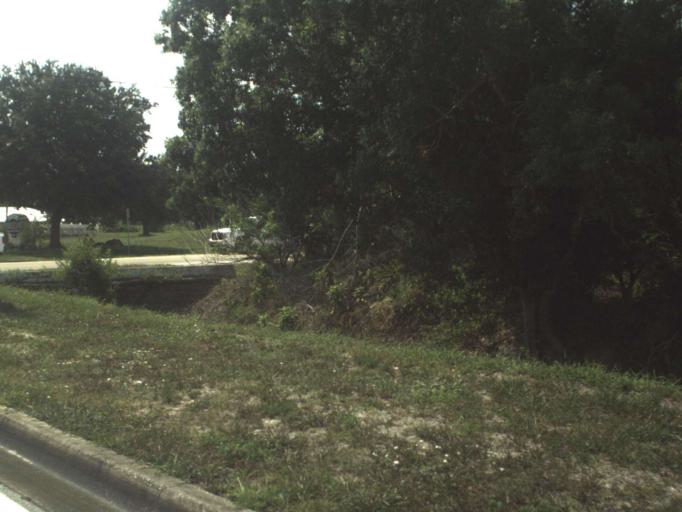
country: US
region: Florida
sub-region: Indian River County
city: Vero Beach
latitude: 27.6460
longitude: -80.4305
